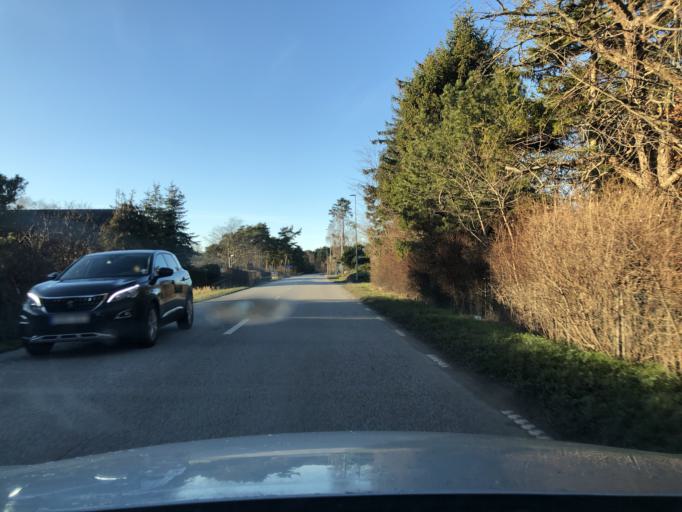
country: SE
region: Skane
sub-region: Trelleborgs Kommun
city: Anderslov
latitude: 55.3455
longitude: 13.2826
